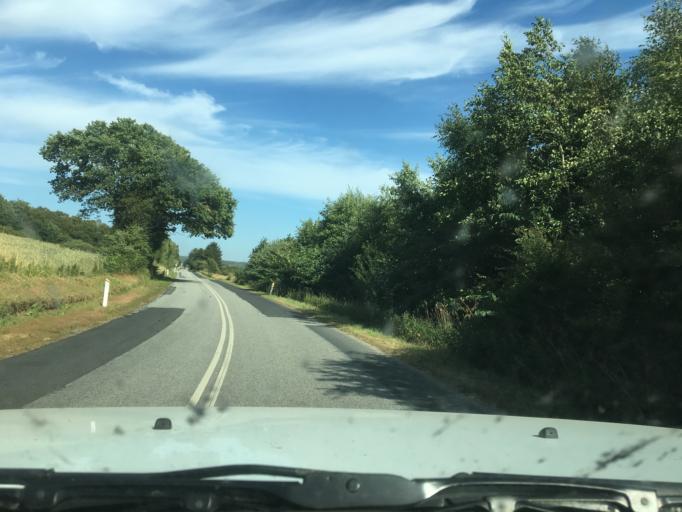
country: DK
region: Central Jutland
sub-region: Viborg Kommune
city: Viborg
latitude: 56.4399
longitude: 9.5077
